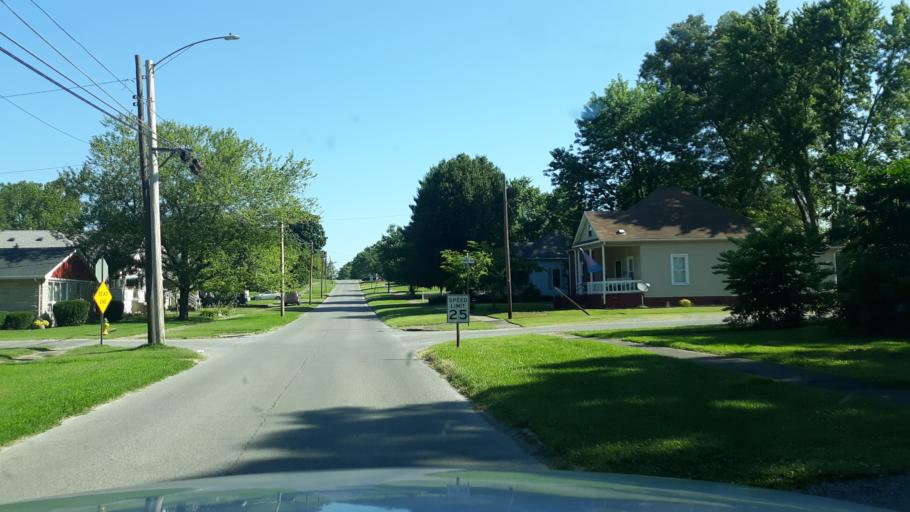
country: US
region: Illinois
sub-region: Saline County
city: Eldorado
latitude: 37.8175
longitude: -88.4361
